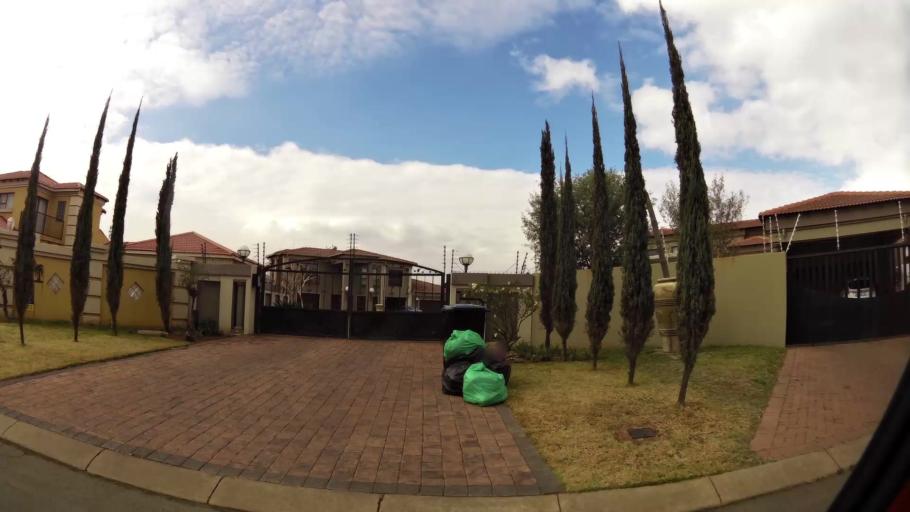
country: ZA
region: Gauteng
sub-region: Sedibeng District Municipality
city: Vanderbijlpark
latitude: -26.7280
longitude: 27.8703
